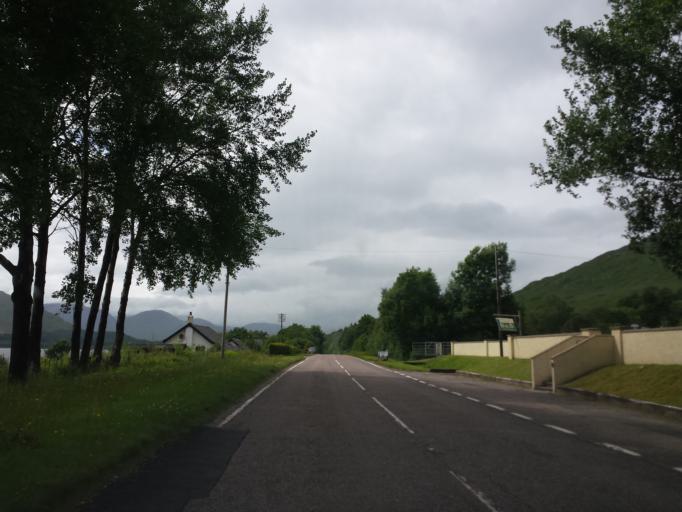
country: GB
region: Scotland
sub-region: Highland
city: Fort William
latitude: 56.8556
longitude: -5.2851
